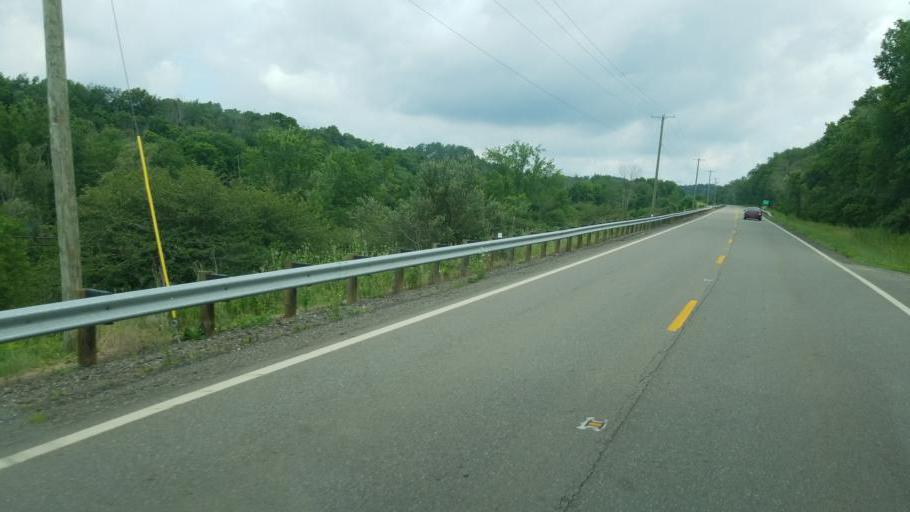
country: US
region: Ohio
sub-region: Columbiana County
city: Lisbon
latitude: 40.7369
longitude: -80.7892
